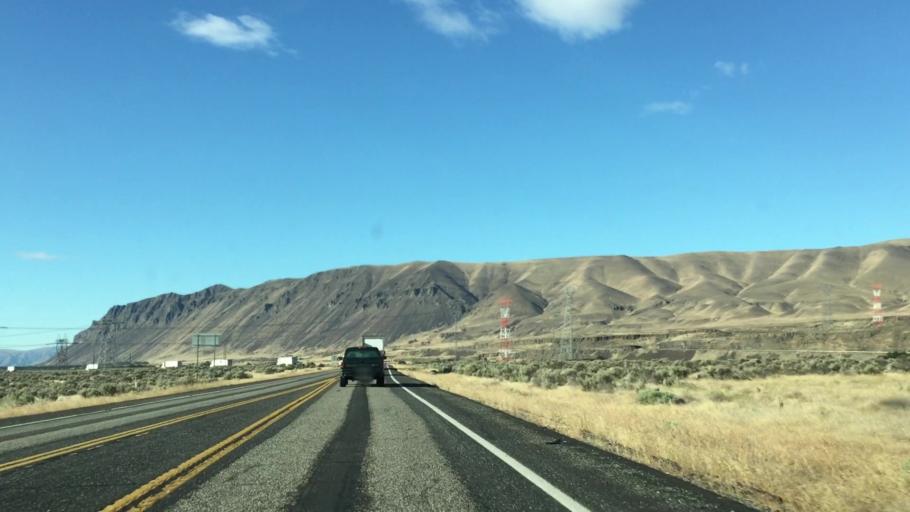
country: US
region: Washington
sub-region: Grant County
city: Mattawa
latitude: 46.8743
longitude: -119.9560
